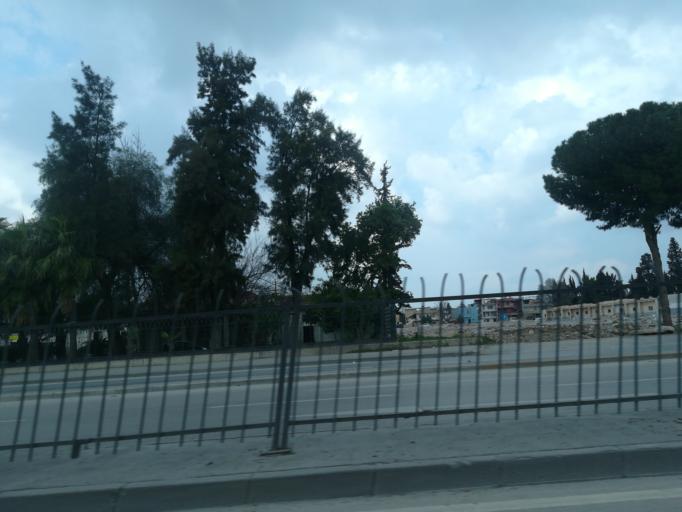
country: TR
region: Adana
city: Seyhan
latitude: 36.9936
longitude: 35.2964
